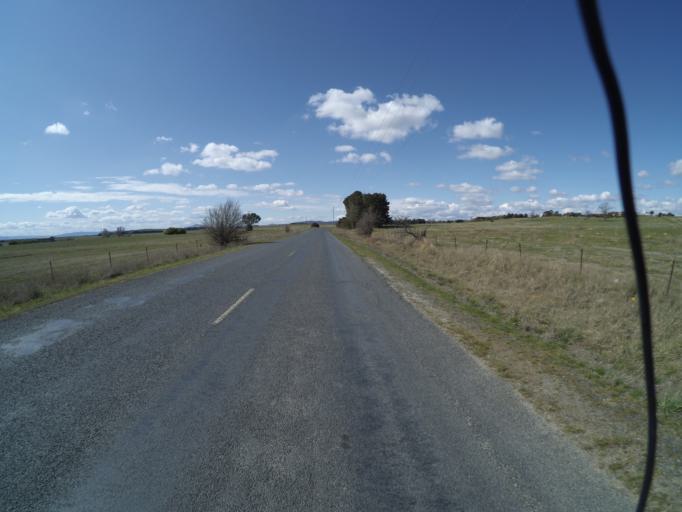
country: AU
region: New South Wales
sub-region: Palerang
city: Bungendore
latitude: -35.2288
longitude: 149.4499
